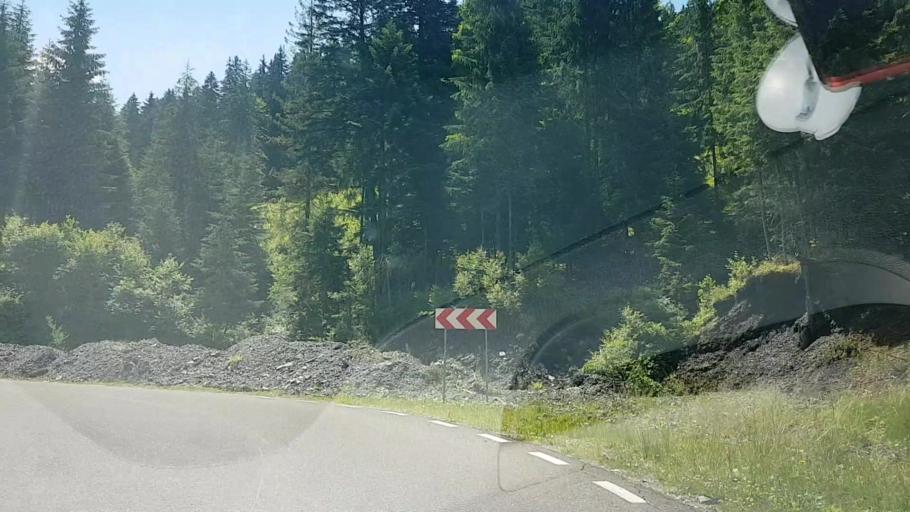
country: RO
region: Suceava
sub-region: Comuna Sadova
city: Sadova
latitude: 47.4641
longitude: 25.5158
